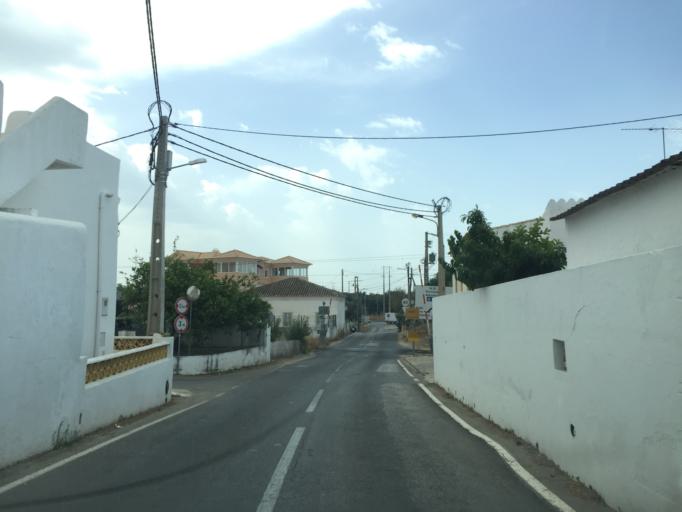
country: PT
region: Faro
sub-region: Loule
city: Almancil
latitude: 37.0985
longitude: -8.0436
